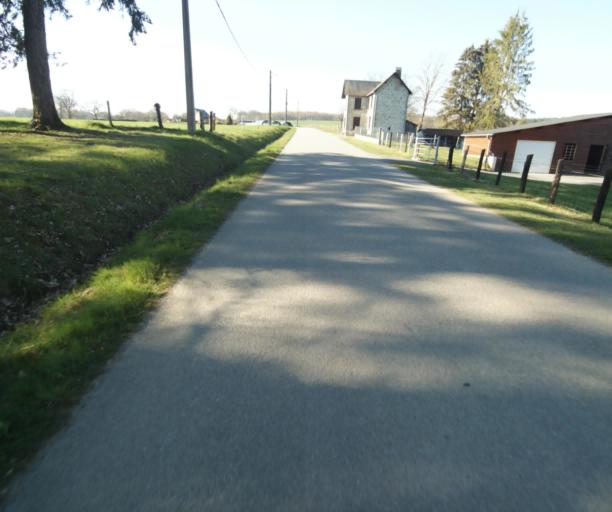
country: FR
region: Limousin
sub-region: Departement de la Correze
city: Chamboulive
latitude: 45.4708
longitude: 1.7219
